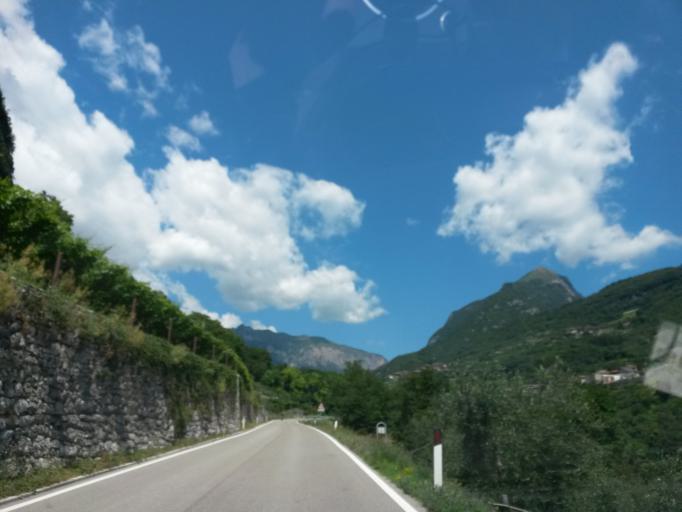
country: IT
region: Trentino-Alto Adige
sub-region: Provincia di Trento
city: Tenno
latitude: 45.9133
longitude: 10.8297
